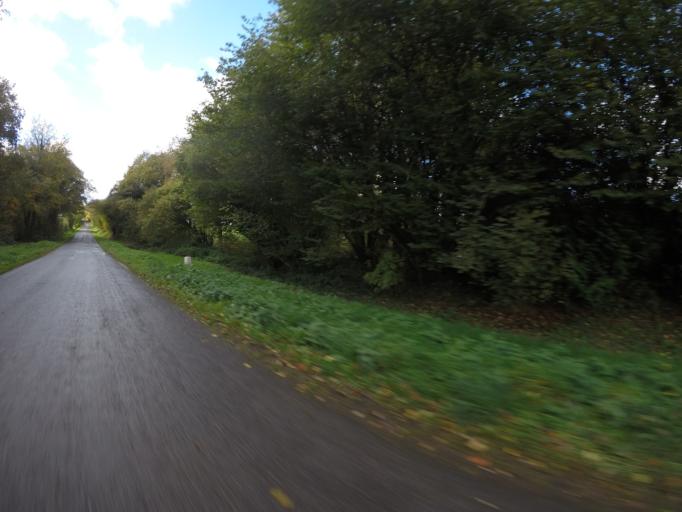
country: FR
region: Brittany
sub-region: Departement des Cotes-d'Armor
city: Bourbriac
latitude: 48.4628
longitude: -3.2488
